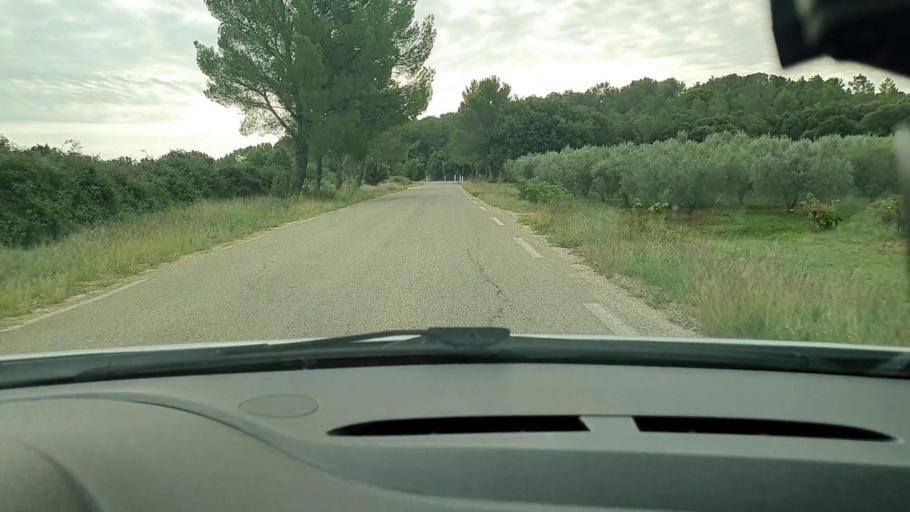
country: FR
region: Languedoc-Roussillon
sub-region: Departement du Gard
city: Montaren-et-Saint-Mediers
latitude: 44.0557
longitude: 4.3278
